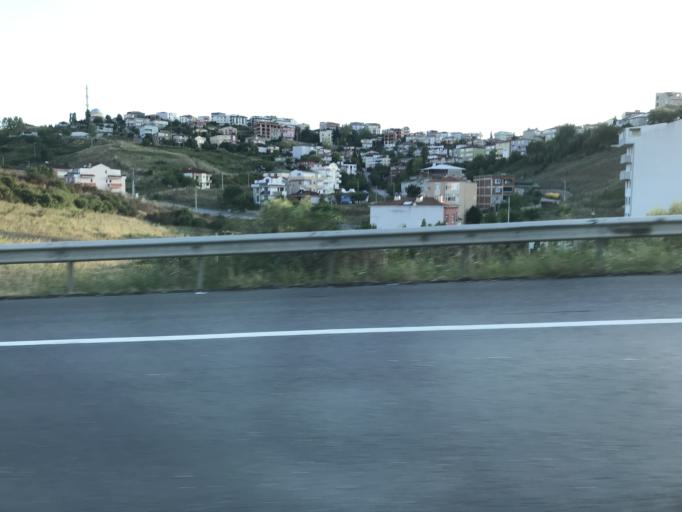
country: TR
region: Kocaeli
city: Darica
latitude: 40.7786
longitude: 29.4182
